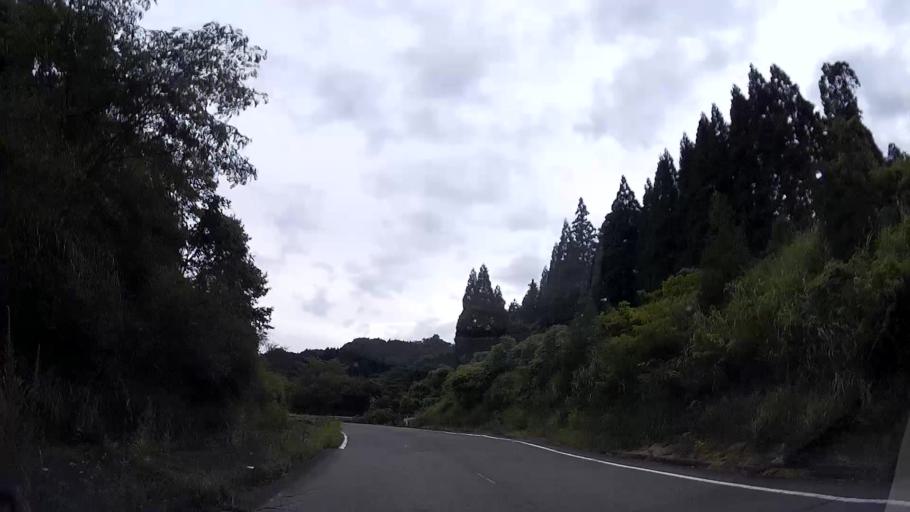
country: JP
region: Oita
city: Hita
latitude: 33.1357
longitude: 130.9862
